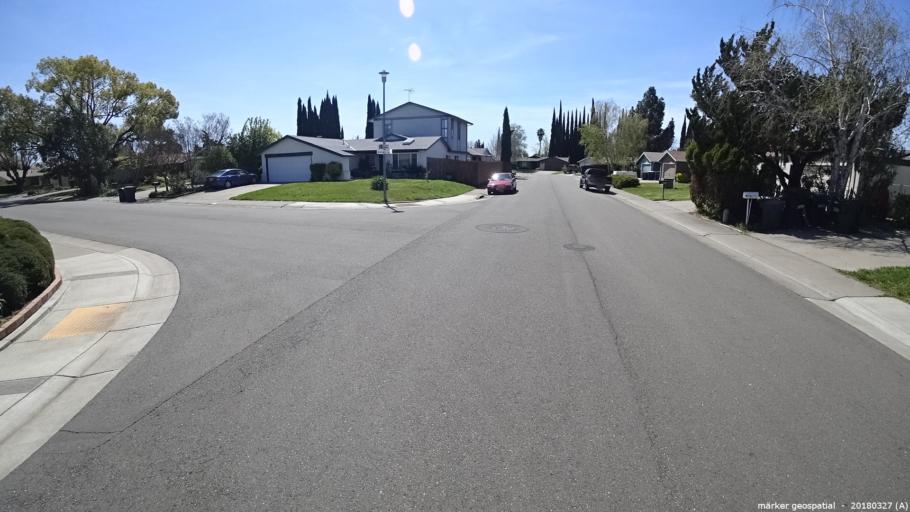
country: US
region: California
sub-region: Sacramento County
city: La Riviera
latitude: 38.5558
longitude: -121.3533
